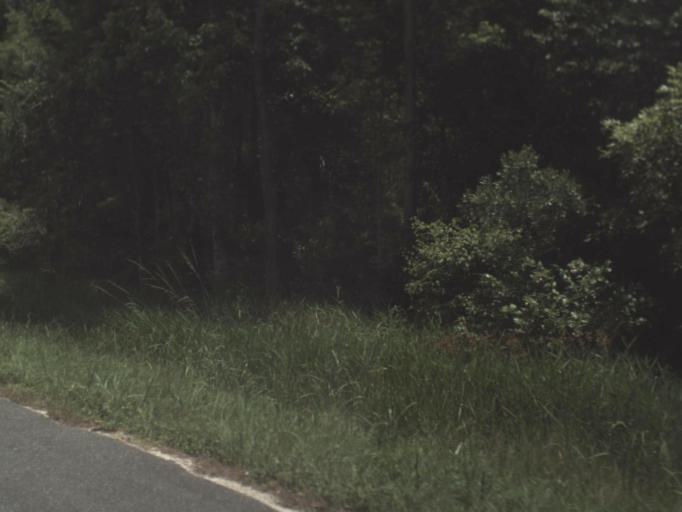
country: US
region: Florida
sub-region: Lafayette County
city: Mayo
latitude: 29.9375
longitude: -83.2698
